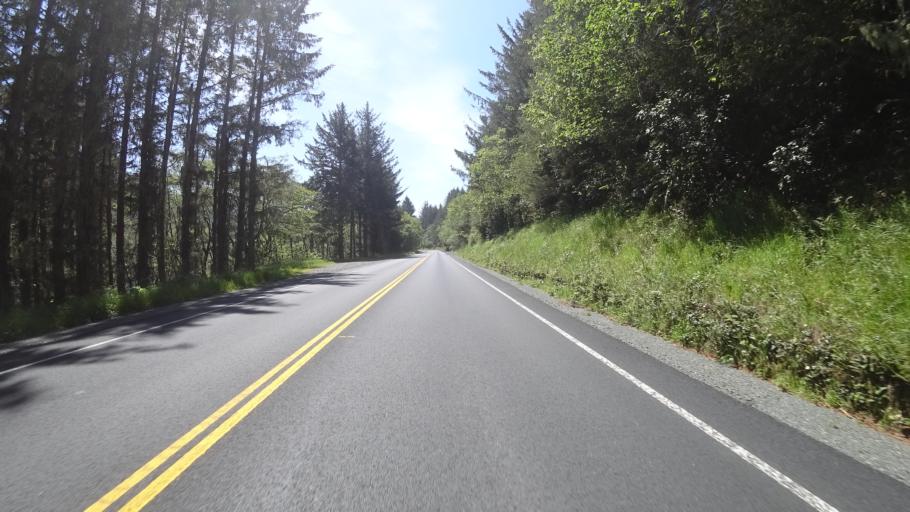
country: US
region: California
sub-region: Humboldt County
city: Westhaven-Moonstone
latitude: 41.2624
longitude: -124.0973
